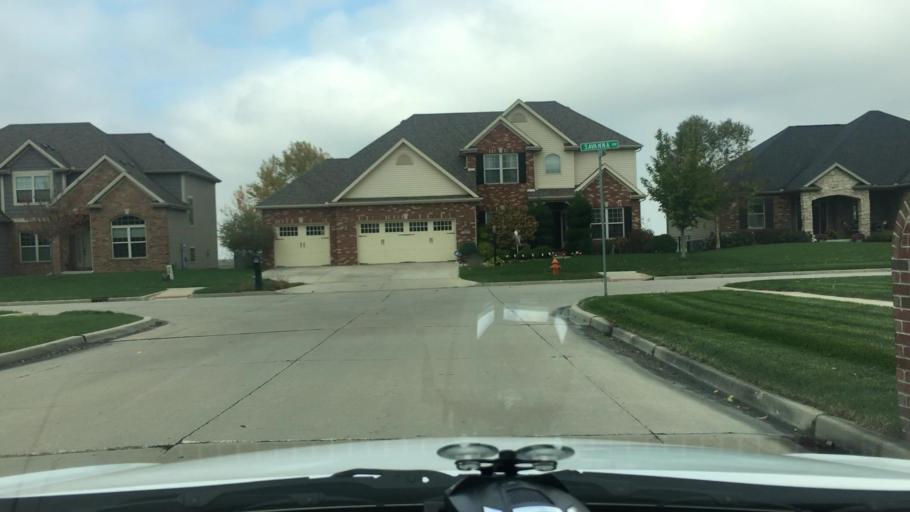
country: US
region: Illinois
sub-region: Champaign County
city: Savoy
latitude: 40.0939
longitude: -88.3275
